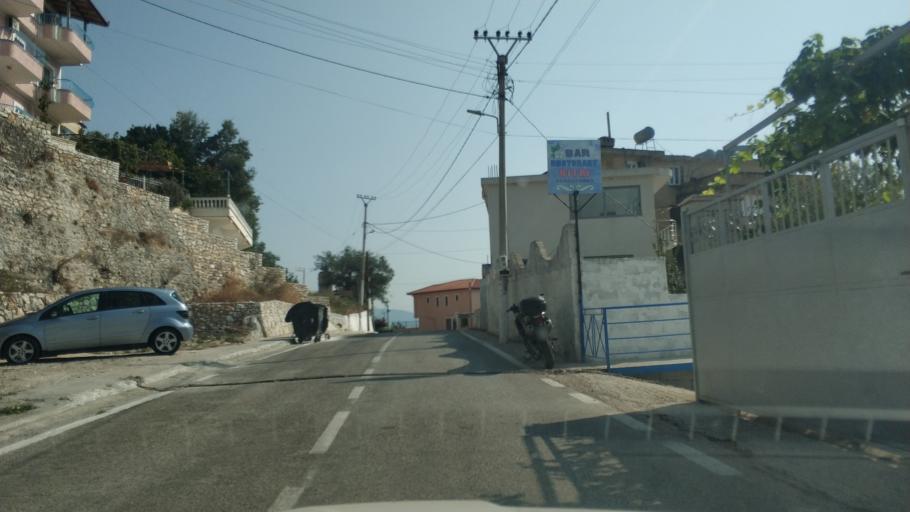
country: AL
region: Vlore
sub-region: Rrethi i Sarandes
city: Lukove
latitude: 40.0170
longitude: 19.8920
